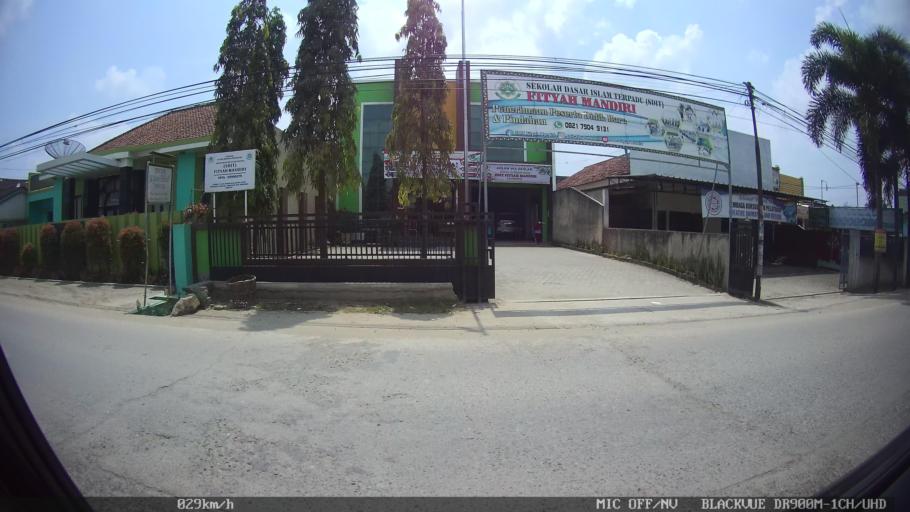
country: ID
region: Lampung
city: Pringsewu
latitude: -5.3455
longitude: 104.9751
